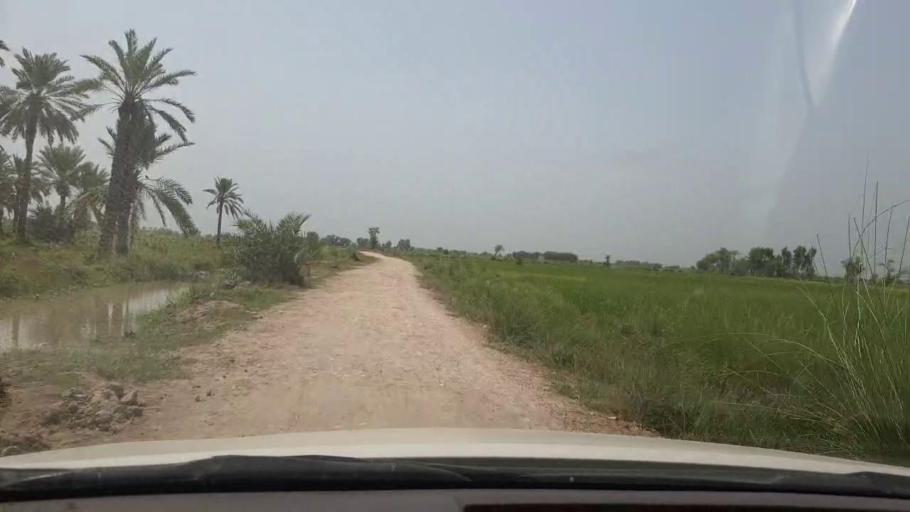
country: PK
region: Sindh
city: Shikarpur
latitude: 28.0175
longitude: 68.6138
